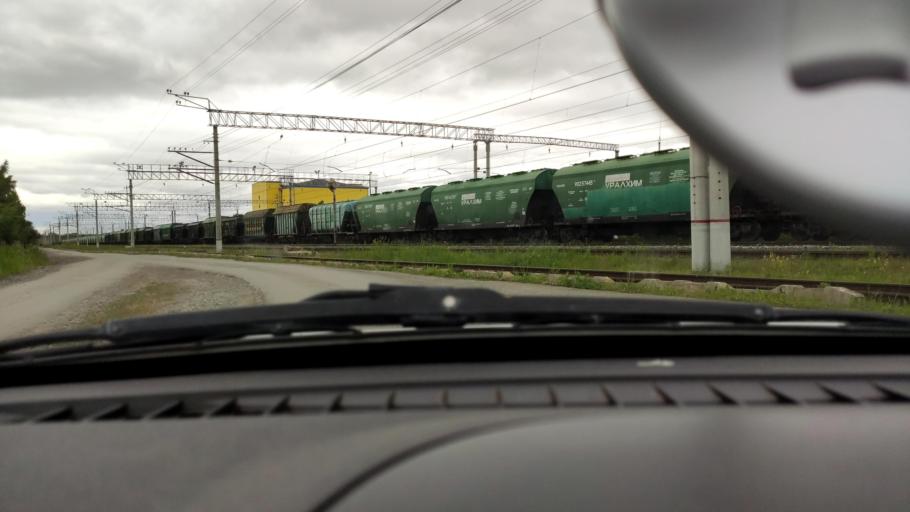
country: RU
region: Perm
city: Ferma
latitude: 57.8890
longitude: 56.2991
